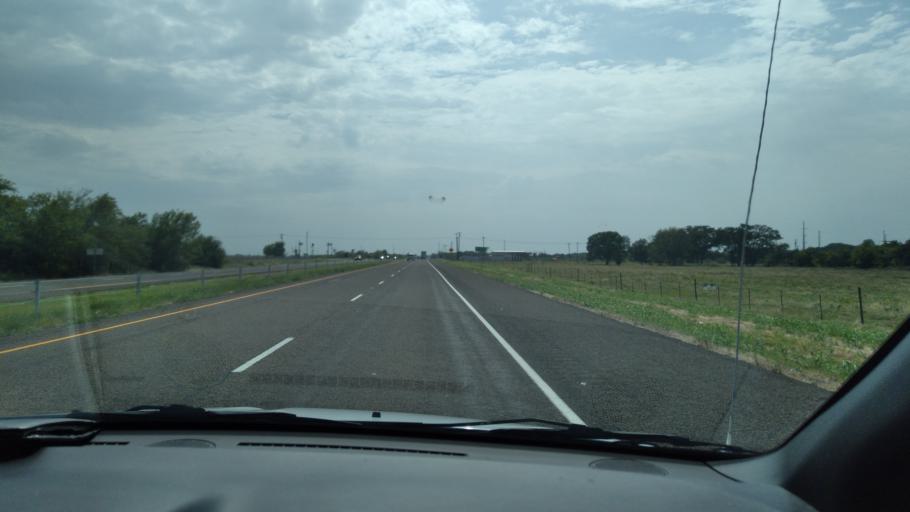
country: US
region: Texas
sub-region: Navarro County
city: Kerens
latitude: 32.1227
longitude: -96.2925
